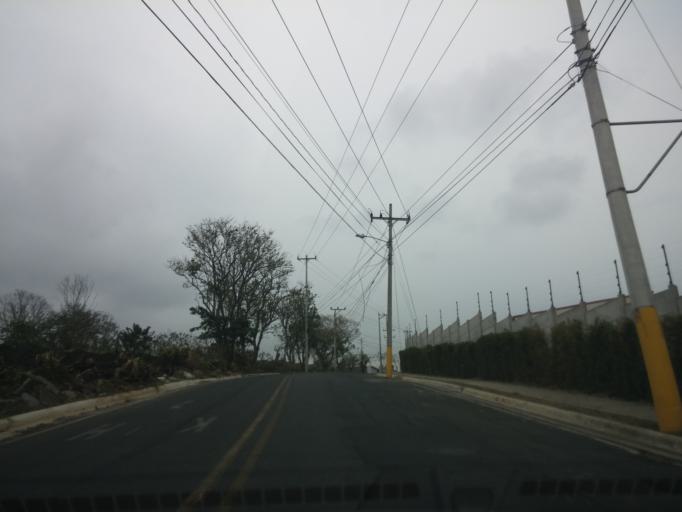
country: CR
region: Heredia
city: San Francisco
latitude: 9.9860
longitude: -84.1436
